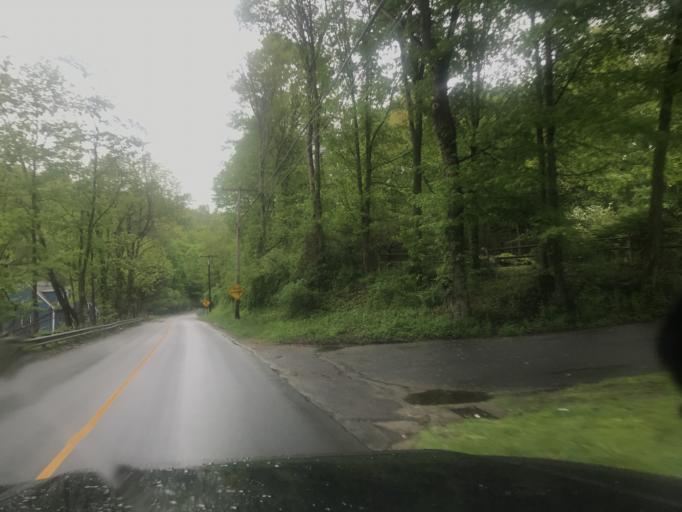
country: US
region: Connecticut
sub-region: Fairfield County
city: Bethel
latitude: 41.3905
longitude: -73.3931
